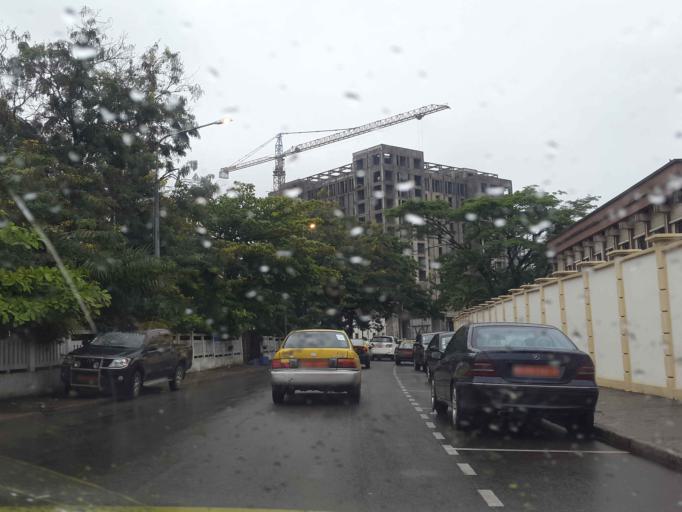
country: CM
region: Littoral
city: Douala
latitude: 4.0436
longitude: 9.6925
